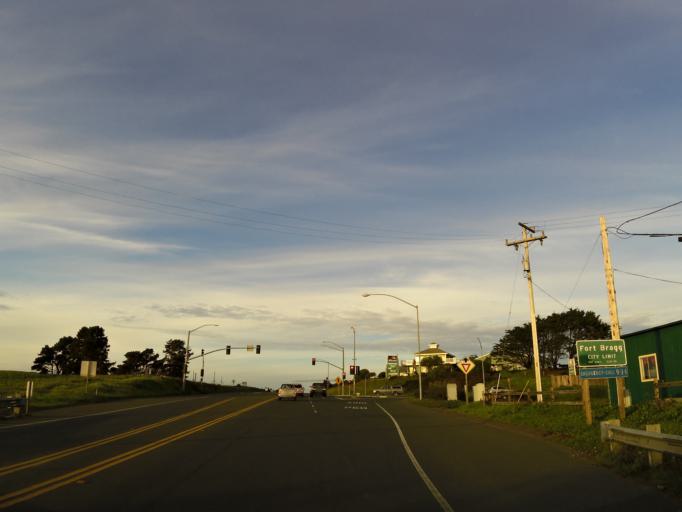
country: US
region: California
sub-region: Mendocino County
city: Fort Bragg
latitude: 39.4194
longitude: -123.8080
